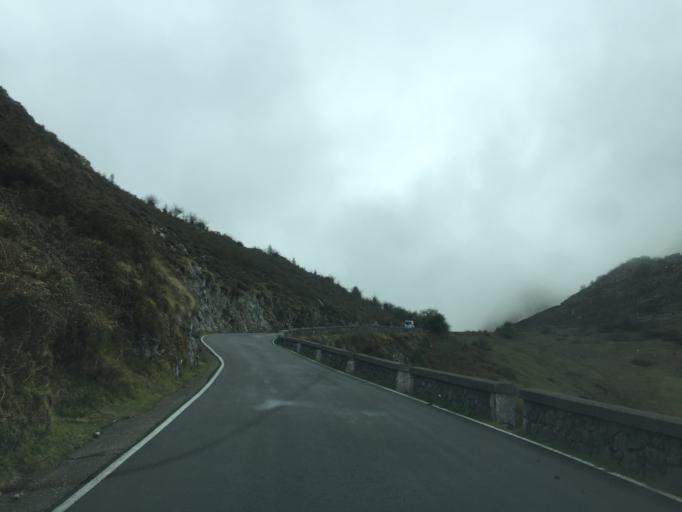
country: ES
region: Asturias
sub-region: Province of Asturias
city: Amieva
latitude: 43.2954
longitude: -5.0153
